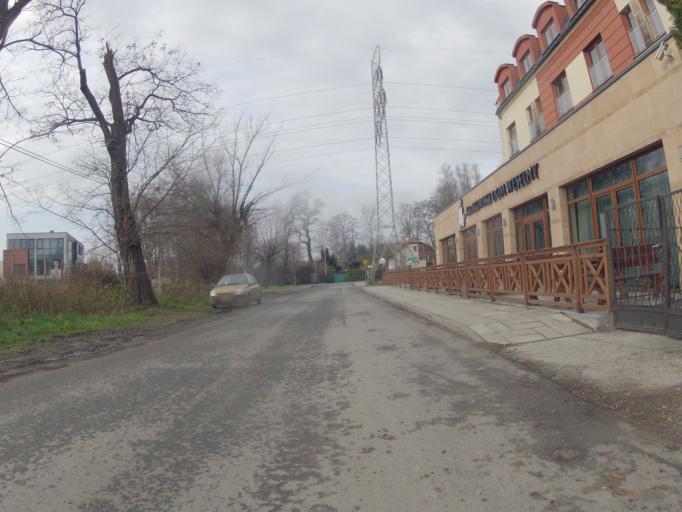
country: PL
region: Lesser Poland Voivodeship
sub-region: Powiat krakowski
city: Rzaska
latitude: 50.0815
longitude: 19.8493
